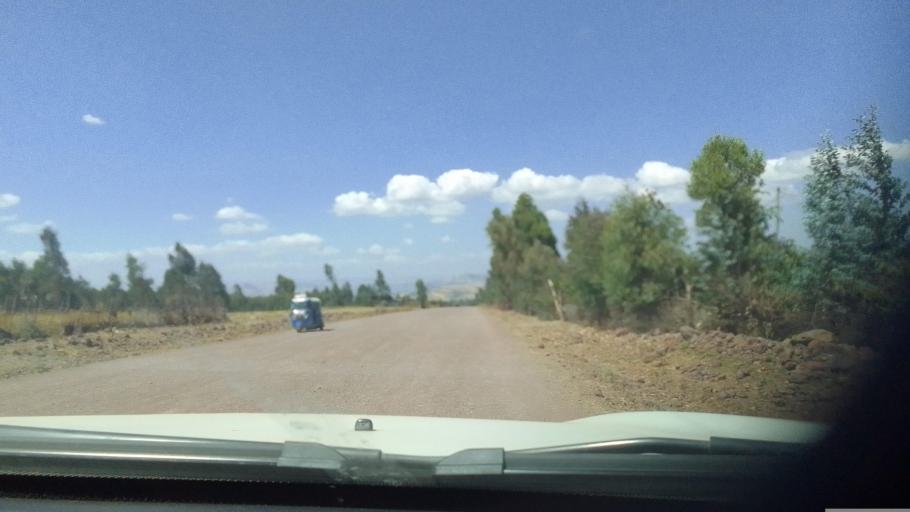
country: ET
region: Oromiya
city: Hagere Hiywet
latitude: 8.9221
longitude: 37.8650
